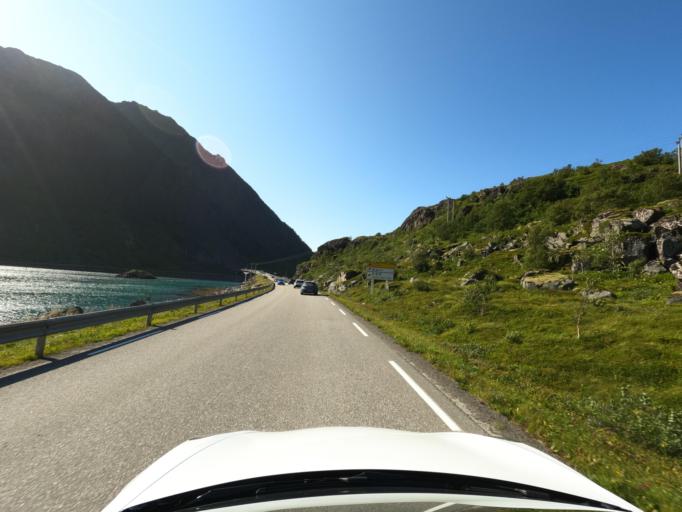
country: NO
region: Nordland
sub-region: Vagan
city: Kabelvag
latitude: 68.2677
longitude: 14.1658
